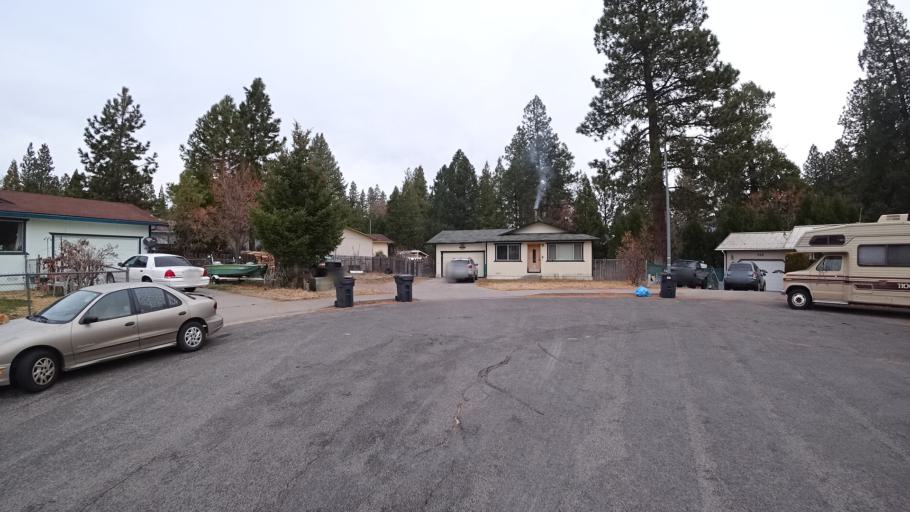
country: US
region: California
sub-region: Siskiyou County
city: Weed
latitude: 41.4171
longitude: -122.3873
